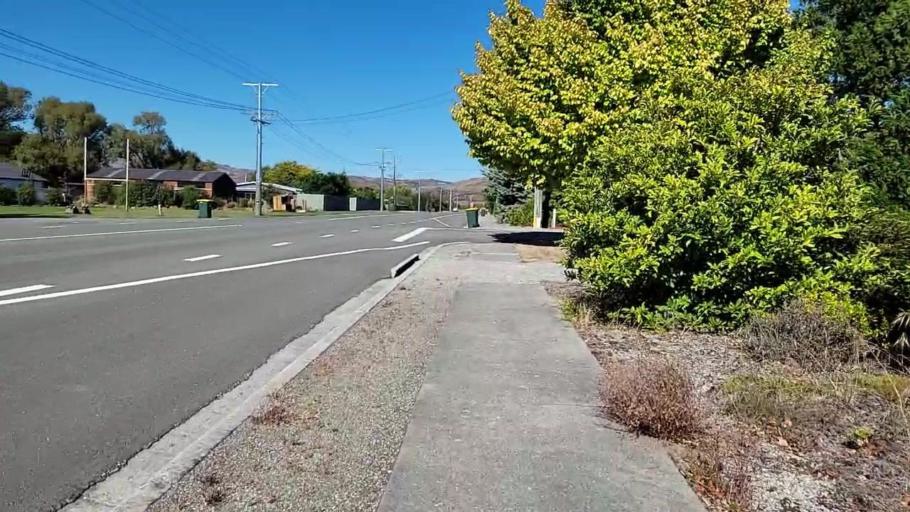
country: NZ
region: Otago
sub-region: Queenstown-Lakes District
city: Wanaka
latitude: -45.1016
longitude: 169.5961
